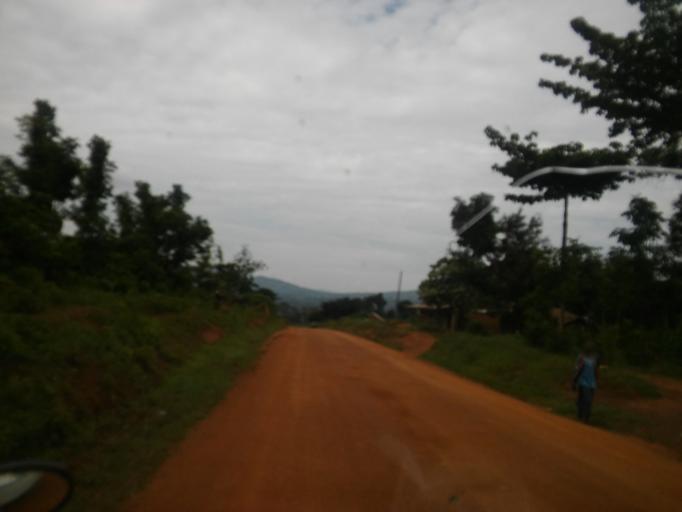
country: UG
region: Eastern Region
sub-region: Mbale District
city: Mbale
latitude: 0.9676
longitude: 34.2090
